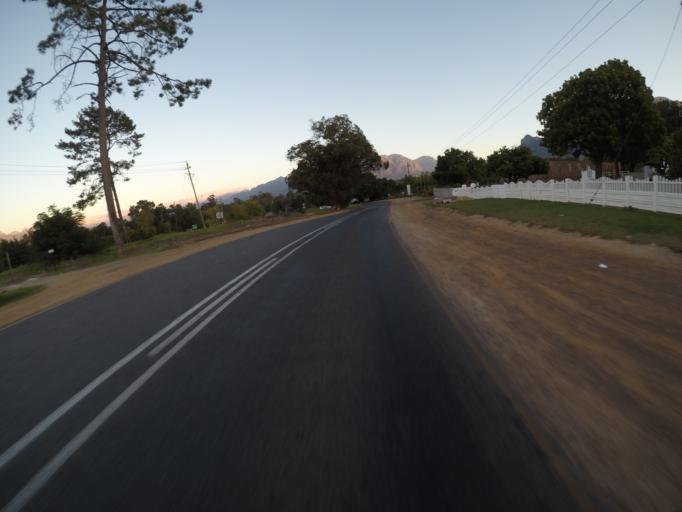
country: ZA
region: Western Cape
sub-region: Cape Winelands District Municipality
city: Paarl
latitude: -33.8358
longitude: 18.9528
